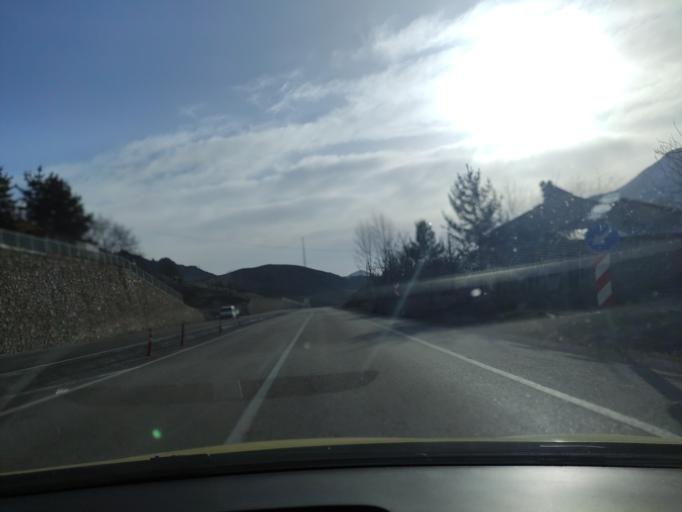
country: TR
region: Gumushane
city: Kale
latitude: 40.4049
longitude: 39.6155
